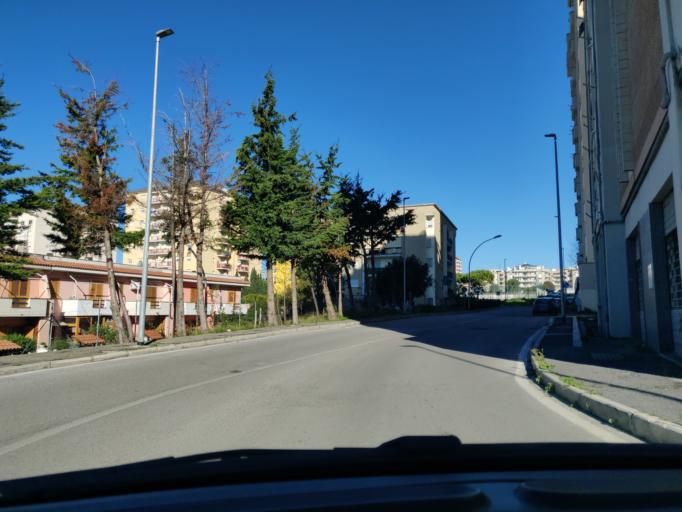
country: IT
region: Latium
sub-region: Citta metropolitana di Roma Capitale
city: Civitavecchia
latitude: 42.0960
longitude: 11.8218
